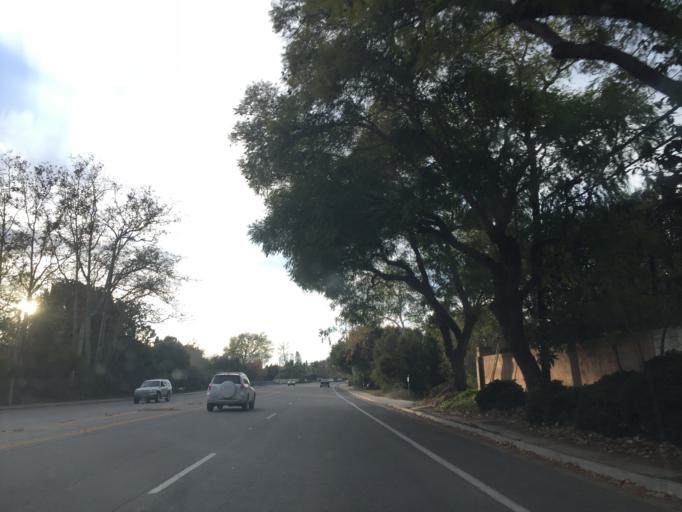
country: US
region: California
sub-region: Santa Barbara County
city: Goleta
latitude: 34.4530
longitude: -119.8118
